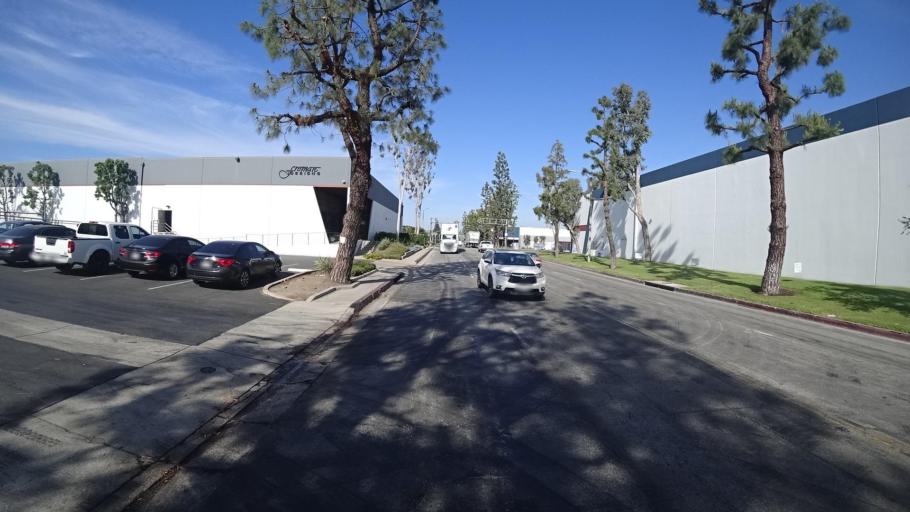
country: US
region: California
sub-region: Los Angeles County
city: South San Jose Hills
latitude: 33.9995
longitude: -117.8929
